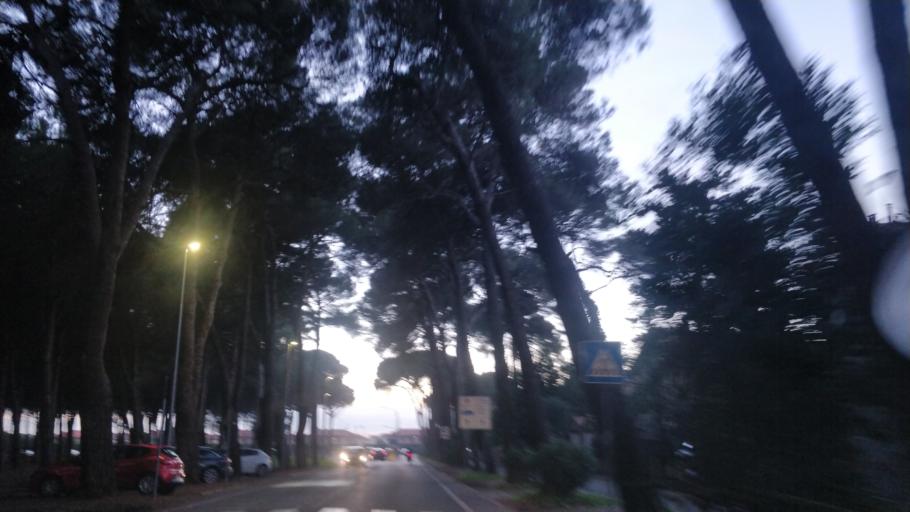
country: IT
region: Tuscany
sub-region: Provincia di Livorno
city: Rosignano Solvay-Castiglioncello
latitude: 43.3880
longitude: 10.4420
